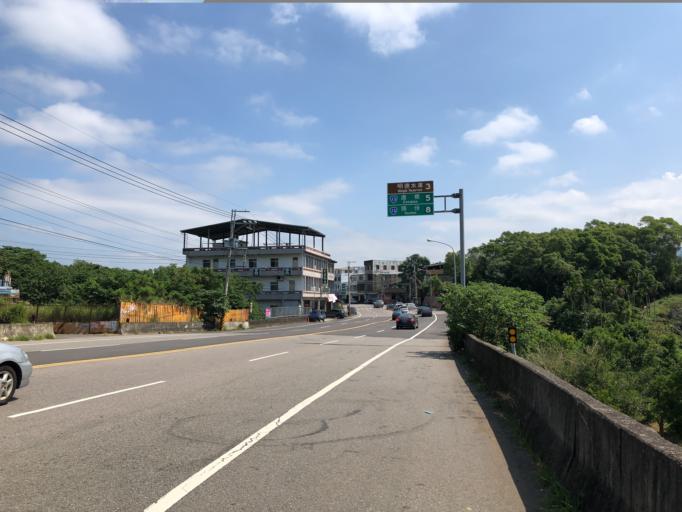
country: TW
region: Taiwan
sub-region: Miaoli
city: Miaoli
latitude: 24.5798
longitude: 120.8623
